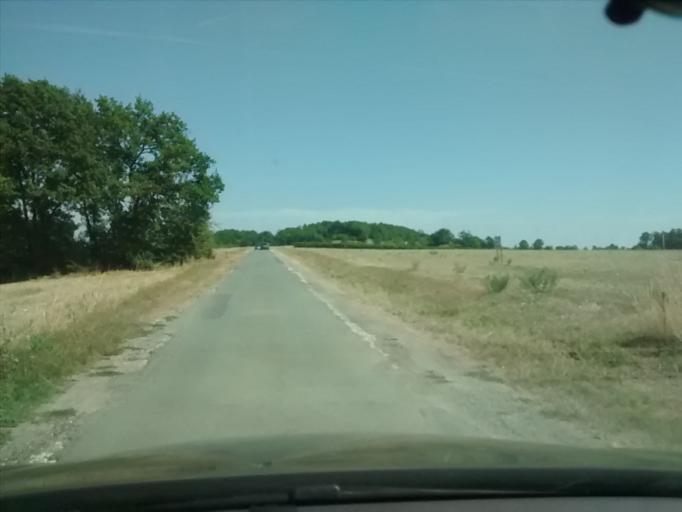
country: FR
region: Aquitaine
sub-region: Departement de la Dordogne
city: Monbazillac
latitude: 44.7641
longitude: 0.4698
